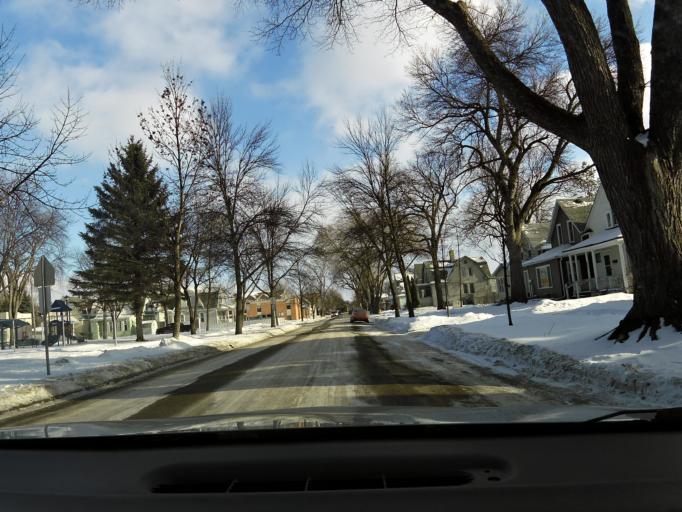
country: US
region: North Dakota
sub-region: Grand Forks County
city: Grand Forks
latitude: 47.9260
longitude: -97.0390
